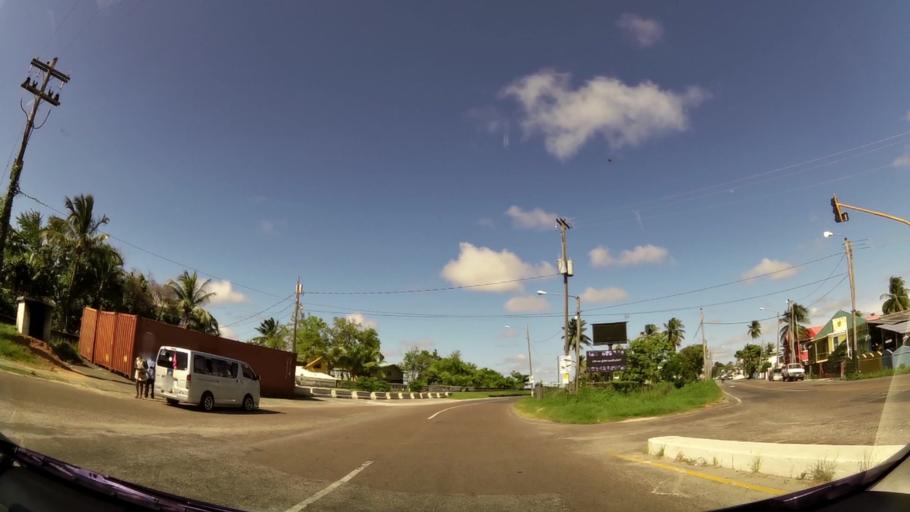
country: GY
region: Demerara-Mahaica
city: Georgetown
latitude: 6.8255
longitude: -58.1430
